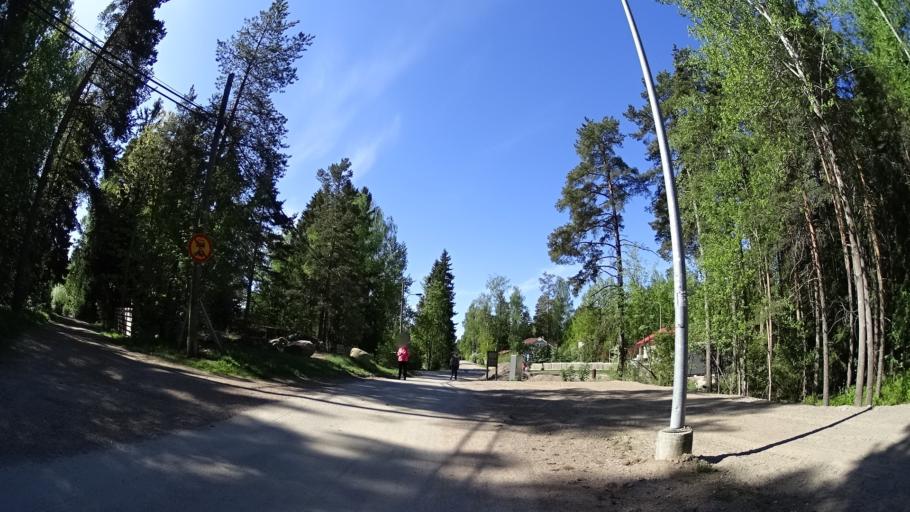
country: FI
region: Uusimaa
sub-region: Helsinki
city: Espoo
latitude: 60.1608
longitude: 24.6682
